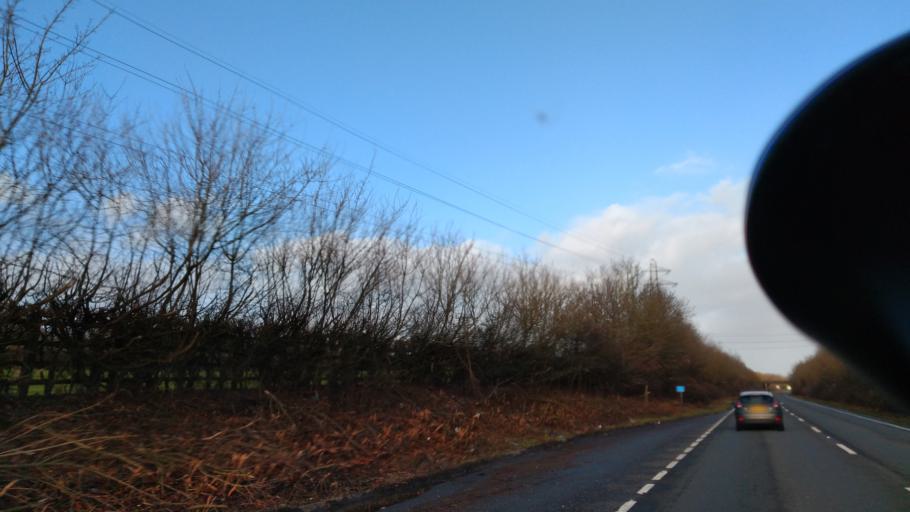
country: GB
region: England
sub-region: Somerset
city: Frome
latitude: 51.2345
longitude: -2.2952
